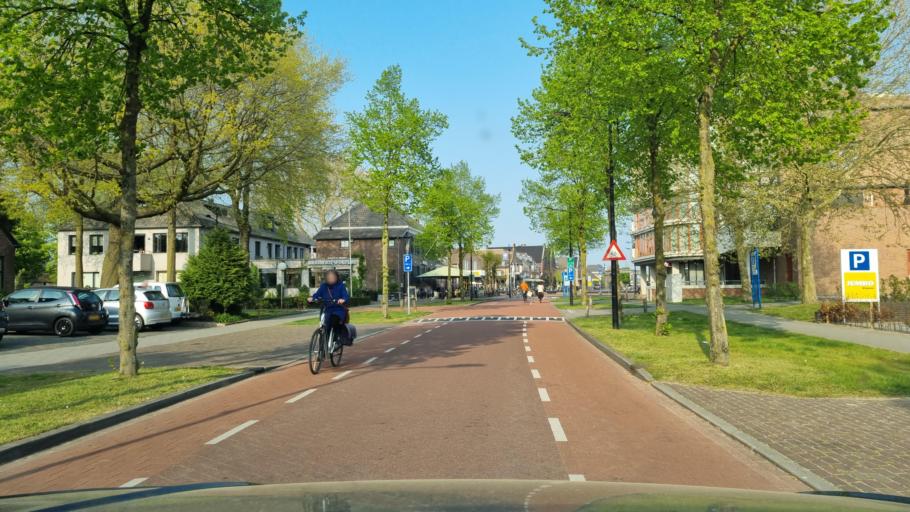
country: NL
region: North Brabant
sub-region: Gemeente Bernheze
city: Heesch
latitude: 51.7349
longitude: 5.5251
